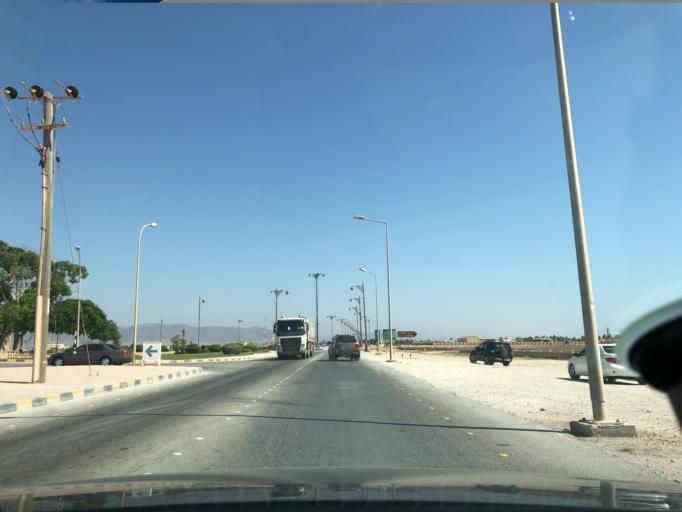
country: OM
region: Zufar
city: Salalah
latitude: 17.0248
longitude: 54.1713
